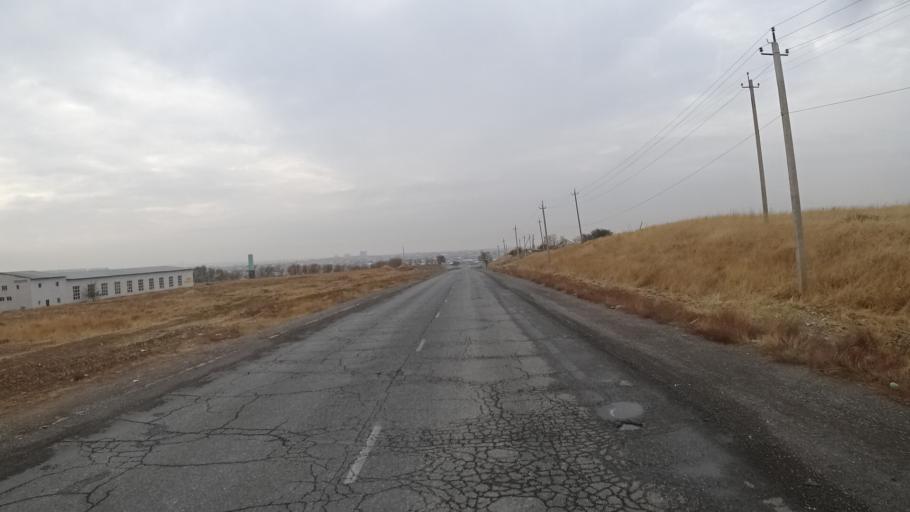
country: KZ
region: Ongtustik Qazaqstan
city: Shymkent
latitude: 42.4126
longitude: 69.6714
